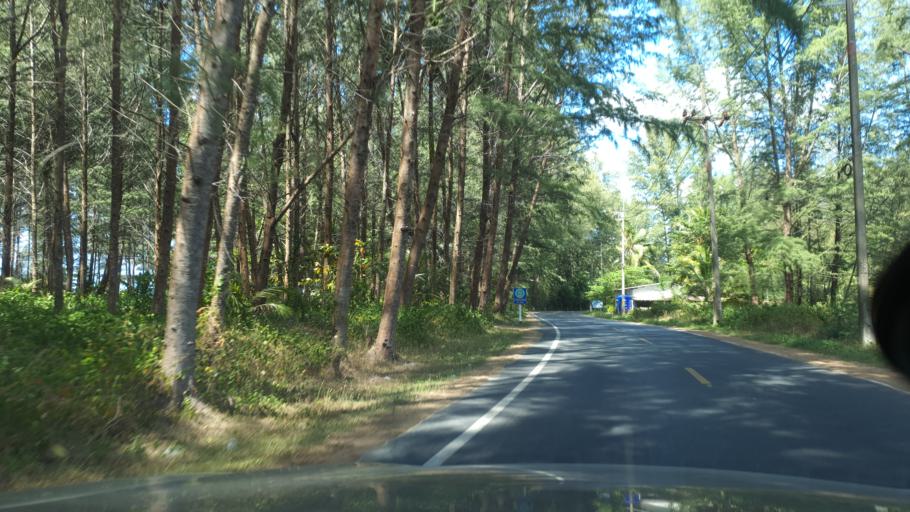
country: TH
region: Phangnga
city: Thai Mueang
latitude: 8.2901
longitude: 98.2743
